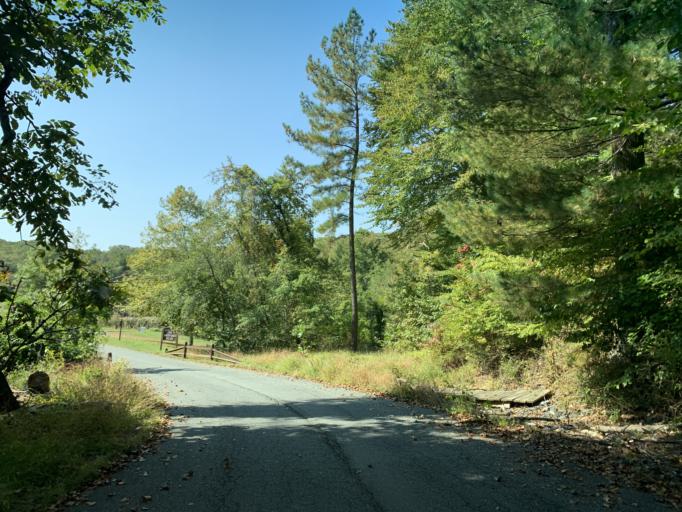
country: US
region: Maryland
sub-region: Harford County
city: Bel Air South
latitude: 39.4876
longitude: -76.3415
